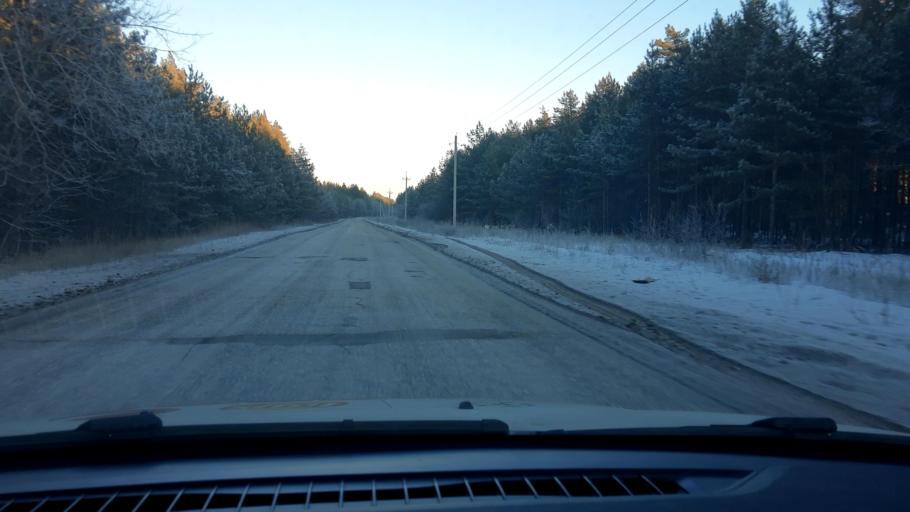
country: RU
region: Nizjnij Novgorod
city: Novosmolinskiy
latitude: 56.3171
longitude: 42.9888
